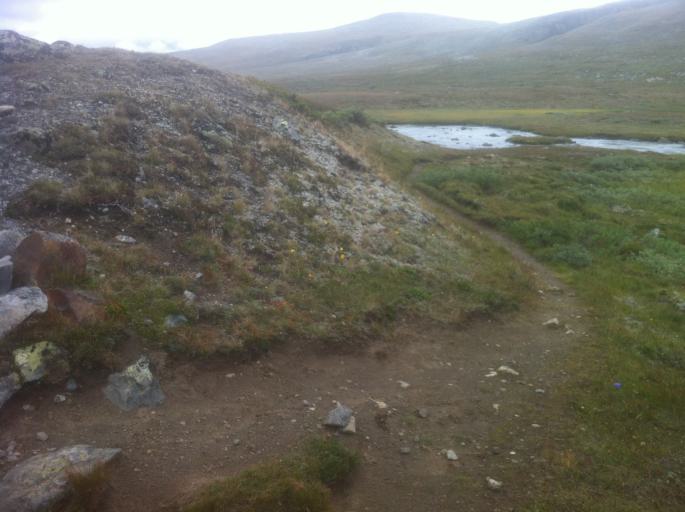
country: NO
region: Oppland
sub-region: Lom
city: Fossbergom
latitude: 61.6213
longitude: 8.6474
